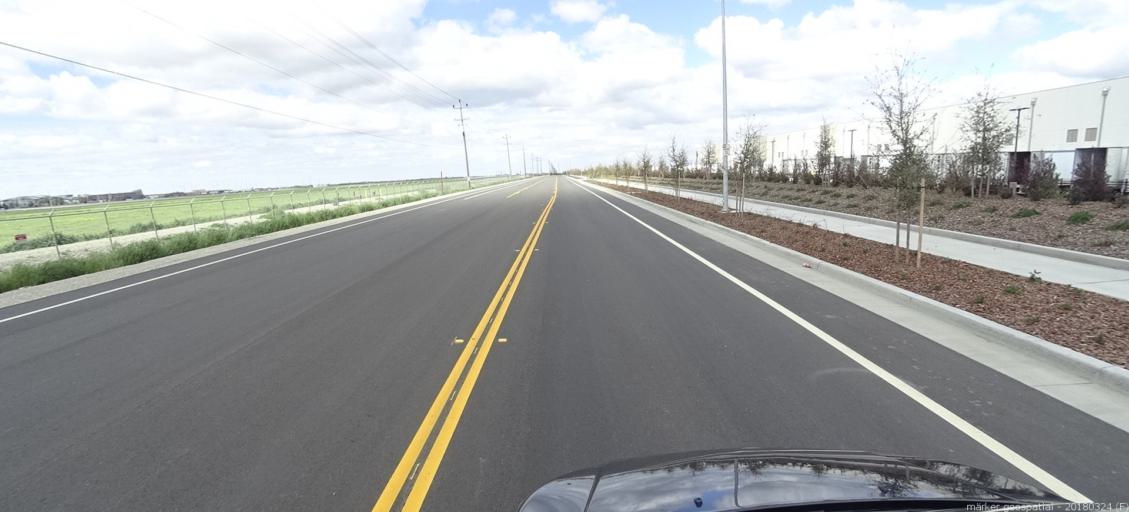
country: US
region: California
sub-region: Yolo County
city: West Sacramento
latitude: 38.6806
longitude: -121.5765
